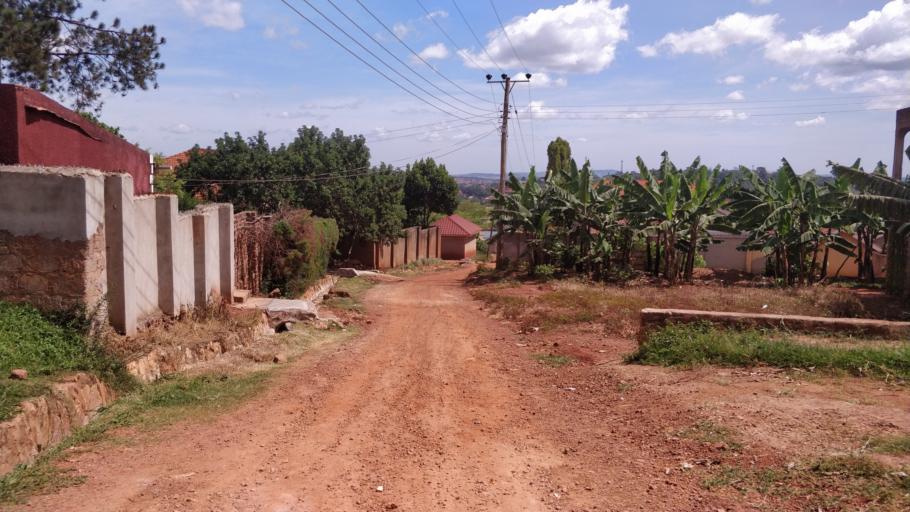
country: UG
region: Central Region
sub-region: Kampala District
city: Kampala
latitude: 0.2677
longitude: 32.6103
